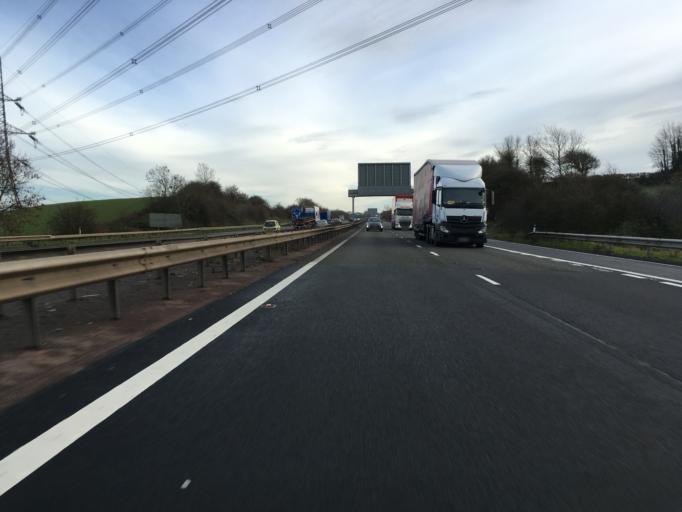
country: GB
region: England
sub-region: South Gloucestershire
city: Almondsbury
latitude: 51.5683
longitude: -2.5747
